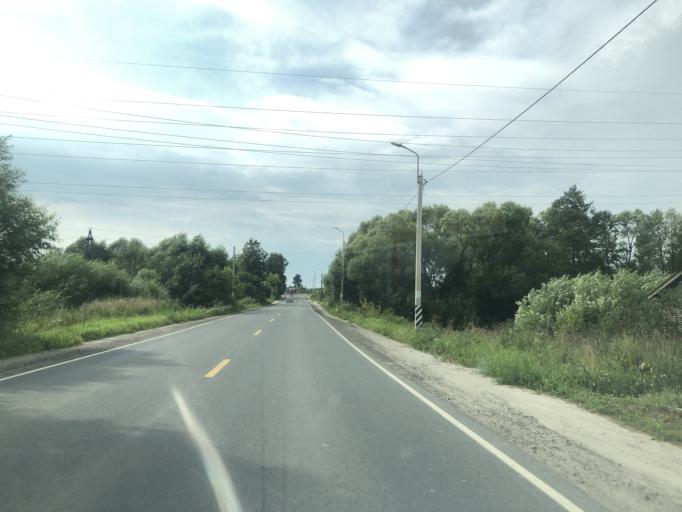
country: RU
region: Ivanovo
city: Shuya
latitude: 56.8543
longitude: 41.5459
